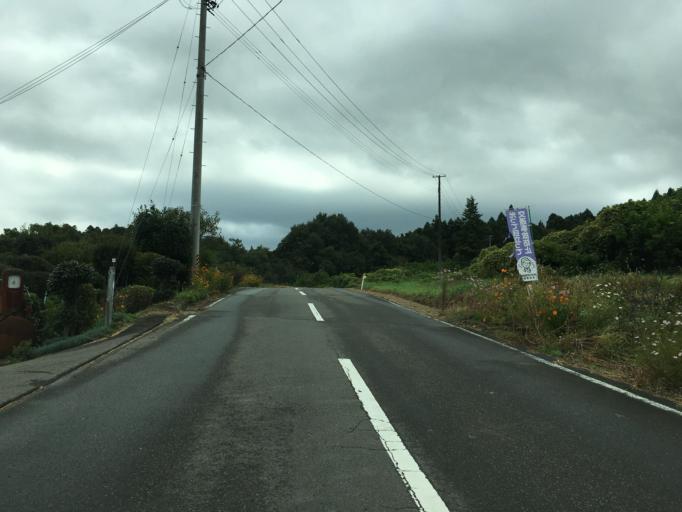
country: JP
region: Fukushima
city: Nihommatsu
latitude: 37.6316
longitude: 140.4372
